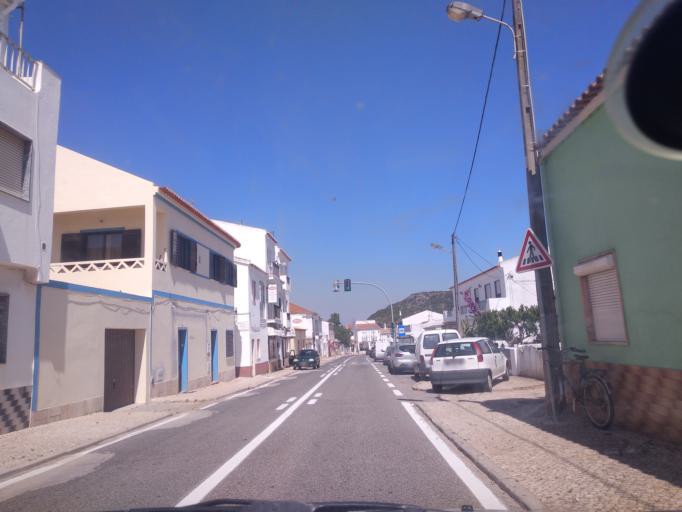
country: PT
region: Faro
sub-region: Lagos
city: Lagos
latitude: 37.1553
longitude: -8.7352
